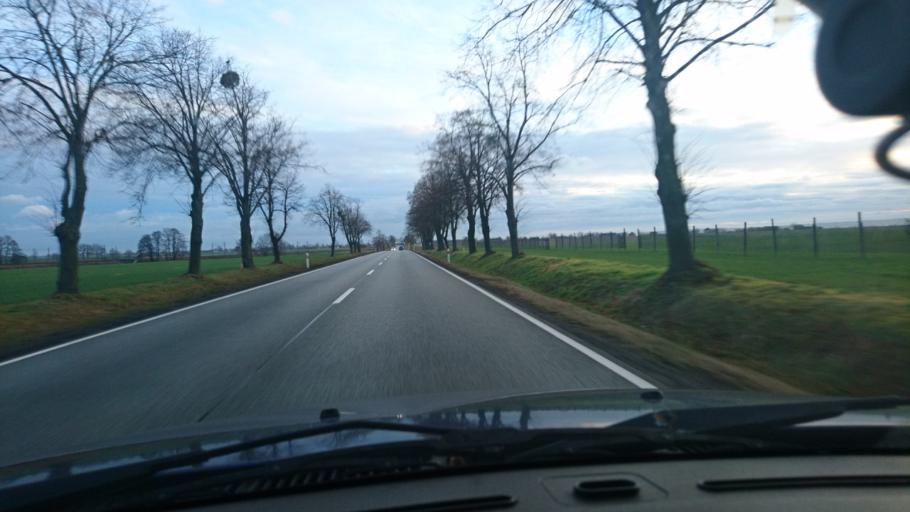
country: PL
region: Opole Voivodeship
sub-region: Powiat kluczborski
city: Kluczbork
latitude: 51.0199
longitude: 18.1965
